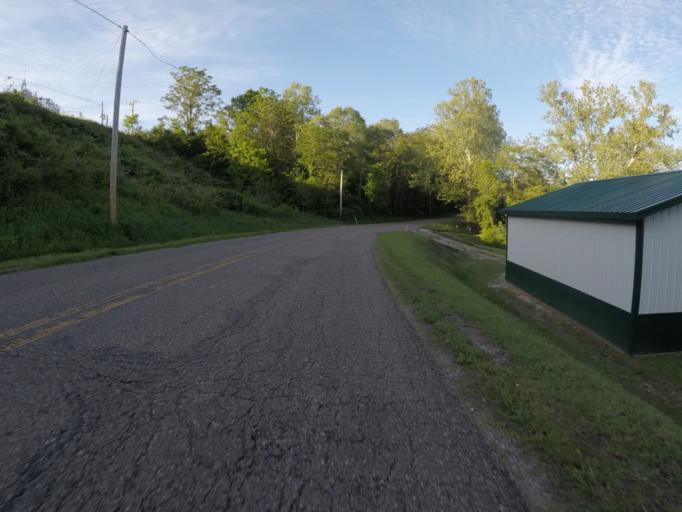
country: US
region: West Virginia
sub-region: Cabell County
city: Huntington
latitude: 38.5092
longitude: -82.4261
